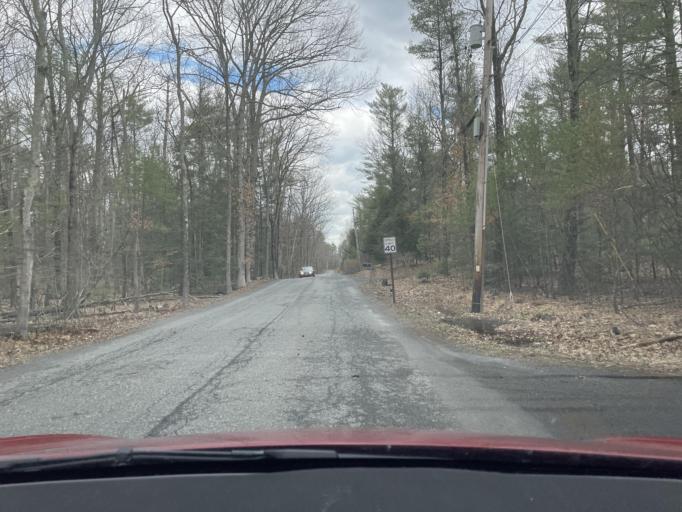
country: US
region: New York
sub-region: Ulster County
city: Zena
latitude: 42.0673
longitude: -74.0351
